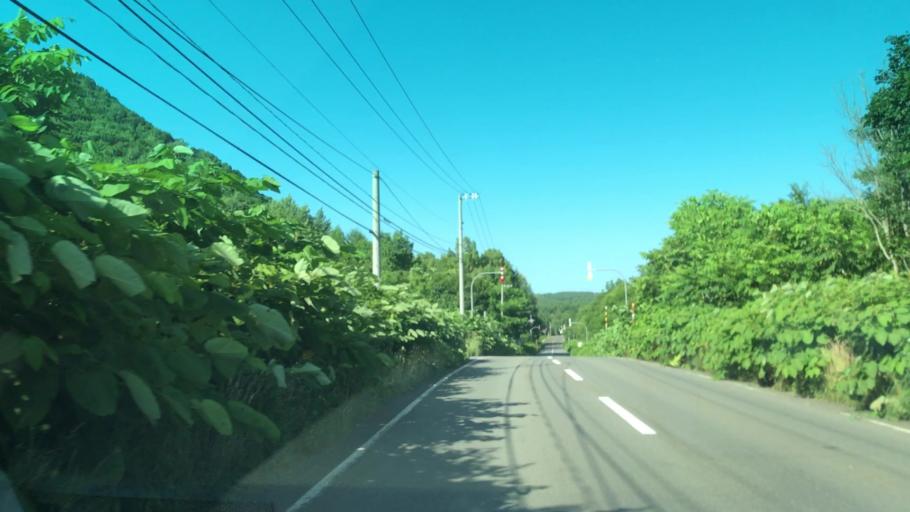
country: JP
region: Hokkaido
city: Yoichi
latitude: 43.0578
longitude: 140.8660
